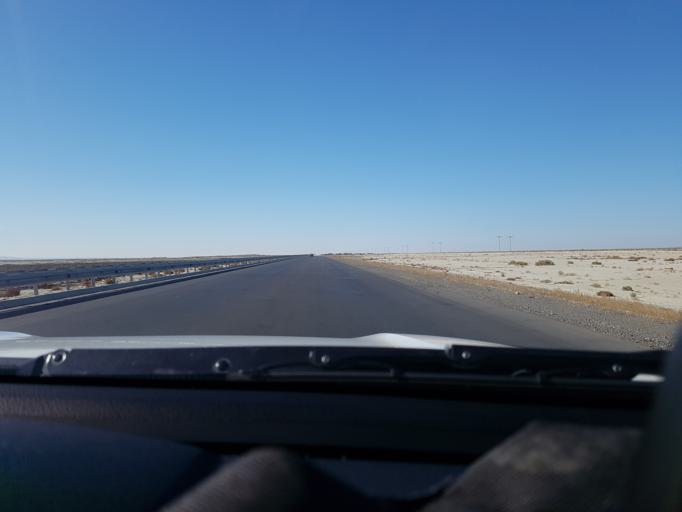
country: TM
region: Balkan
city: Gazanjyk
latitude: 39.2509
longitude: 55.0997
